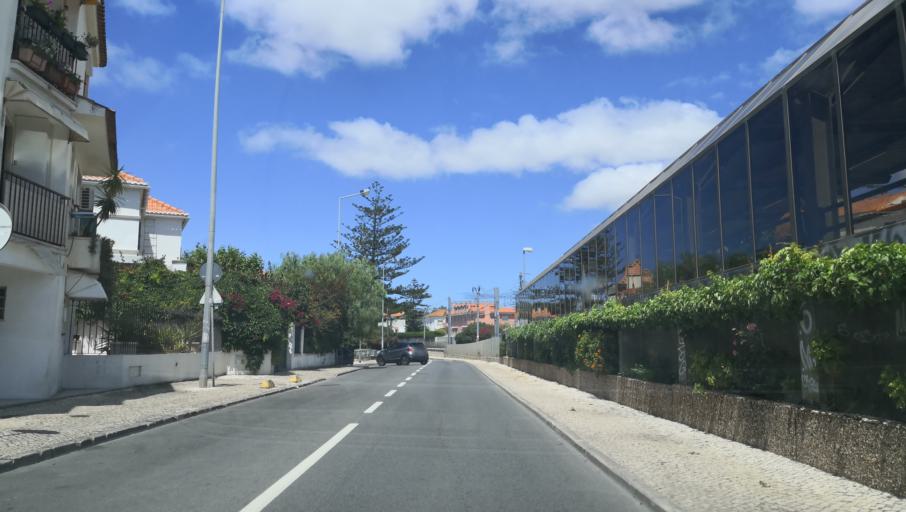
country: PT
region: Lisbon
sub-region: Cascais
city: Parede
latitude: 38.6899
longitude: -9.3572
